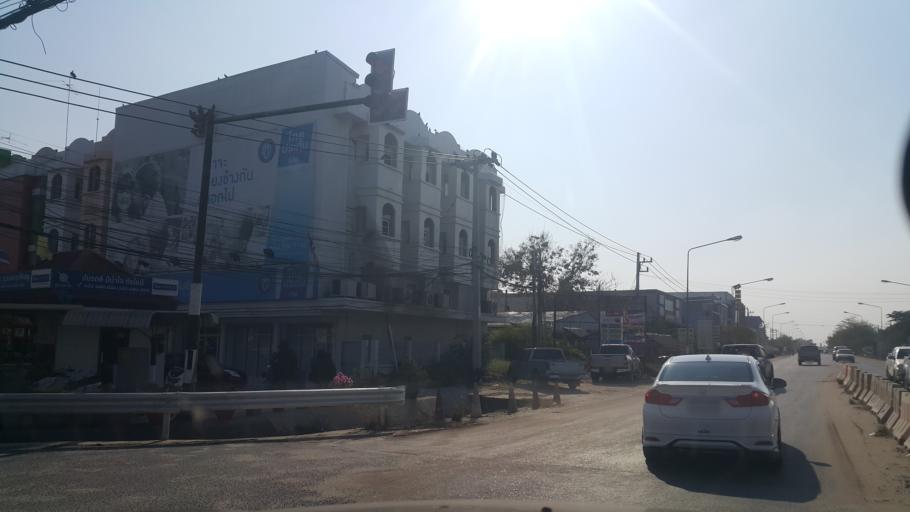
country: TH
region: Nakhon Ratchasima
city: Phimai
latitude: 15.2151
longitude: 102.4855
